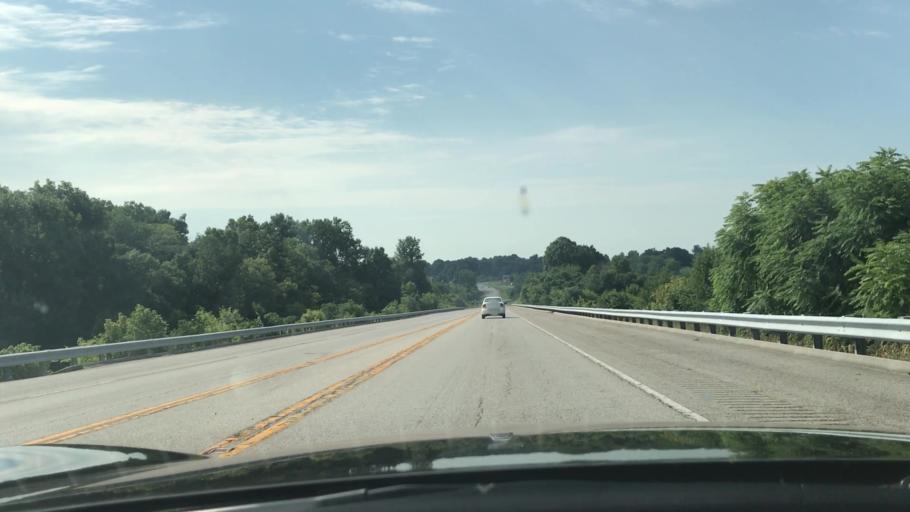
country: US
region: Kentucky
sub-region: Green County
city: Greensburg
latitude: 37.2824
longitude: -85.5159
